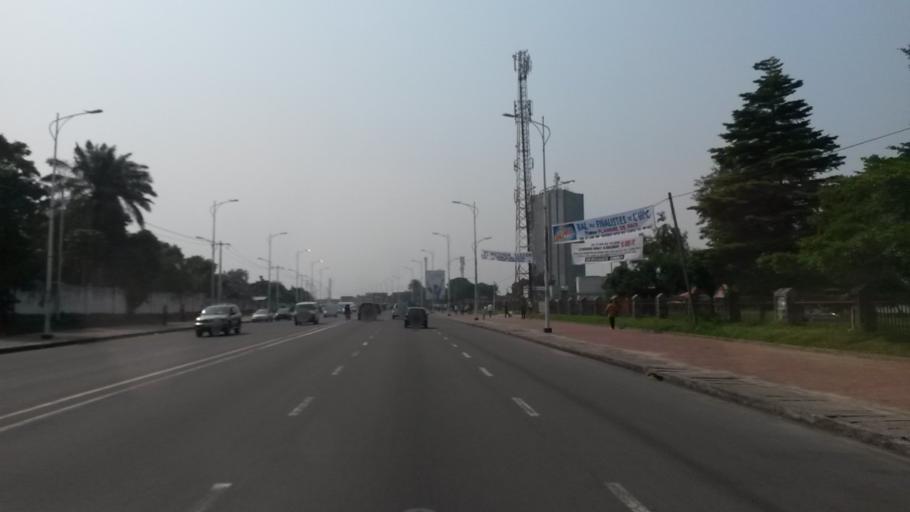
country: CD
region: Kinshasa
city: Kinshasa
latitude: -4.3335
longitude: 15.2965
